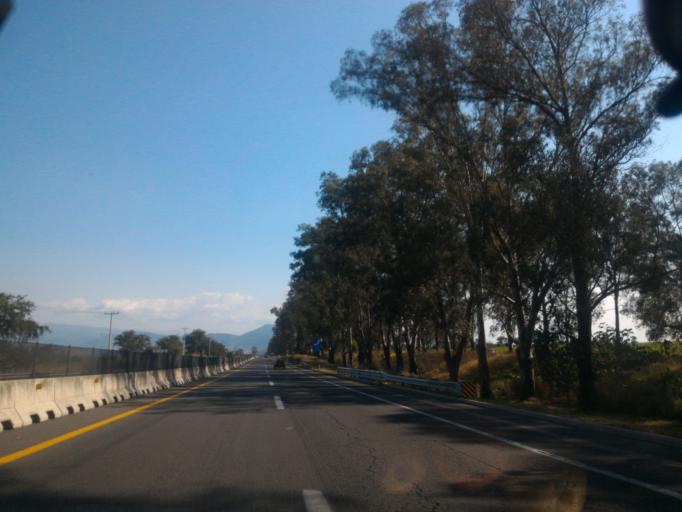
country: MX
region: Jalisco
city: Zapotiltic
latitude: 19.5711
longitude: -103.4444
